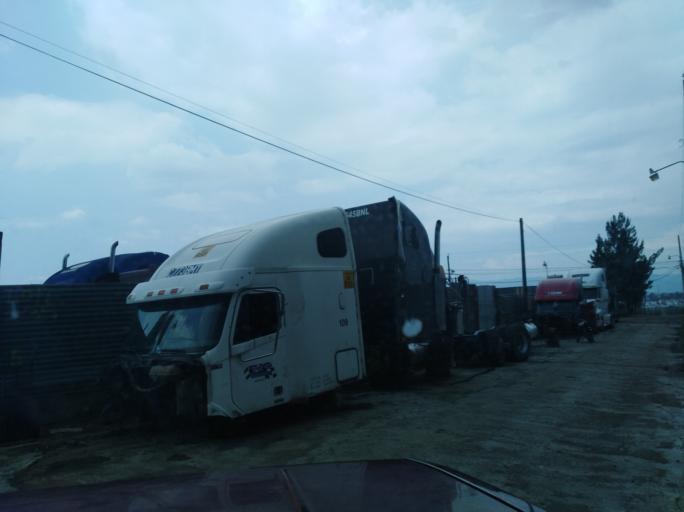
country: GT
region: Guatemala
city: Villa Nueva
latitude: 14.5252
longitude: -90.6231
